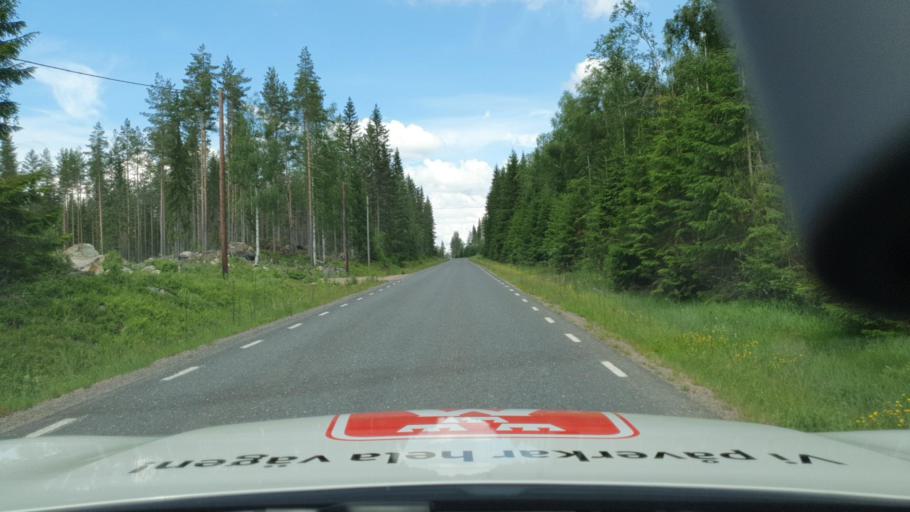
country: SE
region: Vaermland
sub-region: Torsby Kommun
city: Torsby
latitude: 60.5252
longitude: 12.8253
